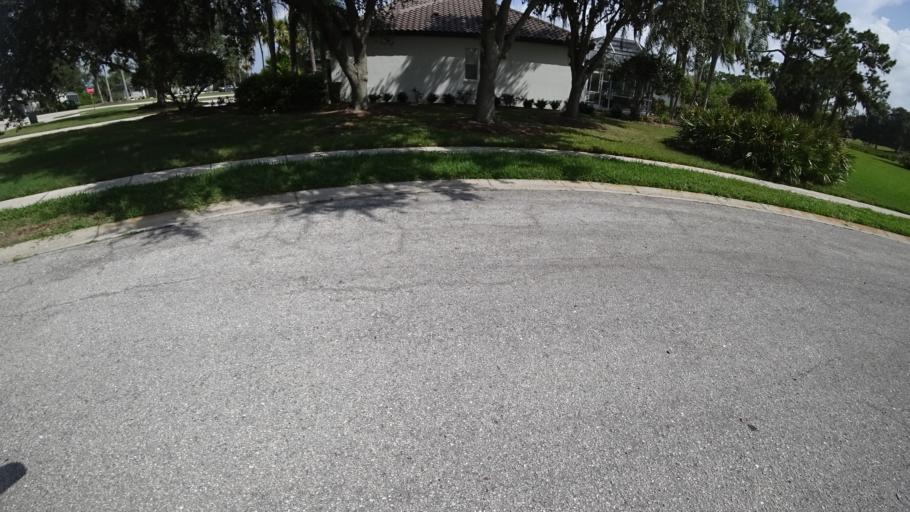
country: US
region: Florida
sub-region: Sarasota County
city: The Meadows
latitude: 27.4141
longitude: -82.4364
